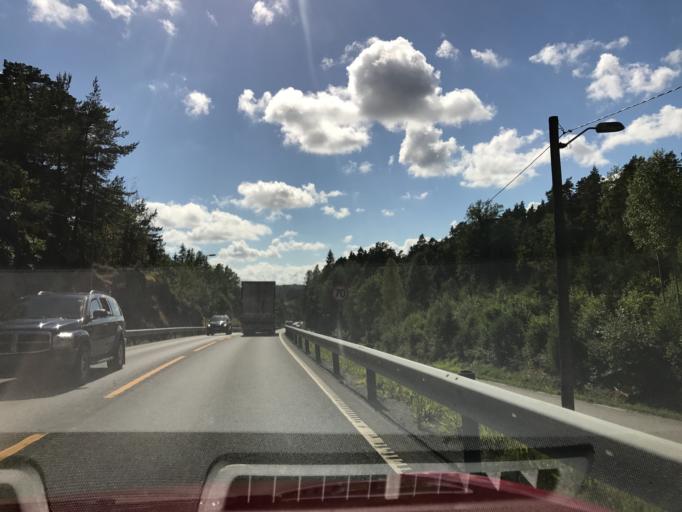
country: NO
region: Telemark
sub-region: Bamble
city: Langesund
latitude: 58.9964
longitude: 9.6469
